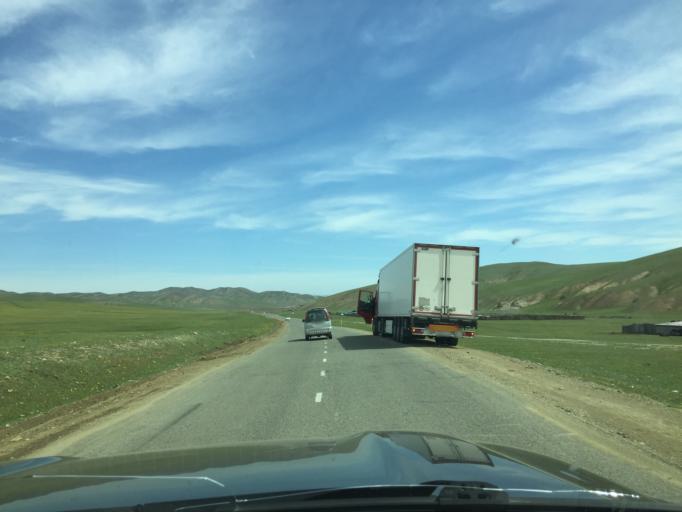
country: MN
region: Central Aimak
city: Bornuur
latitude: 48.6690
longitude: 106.1351
